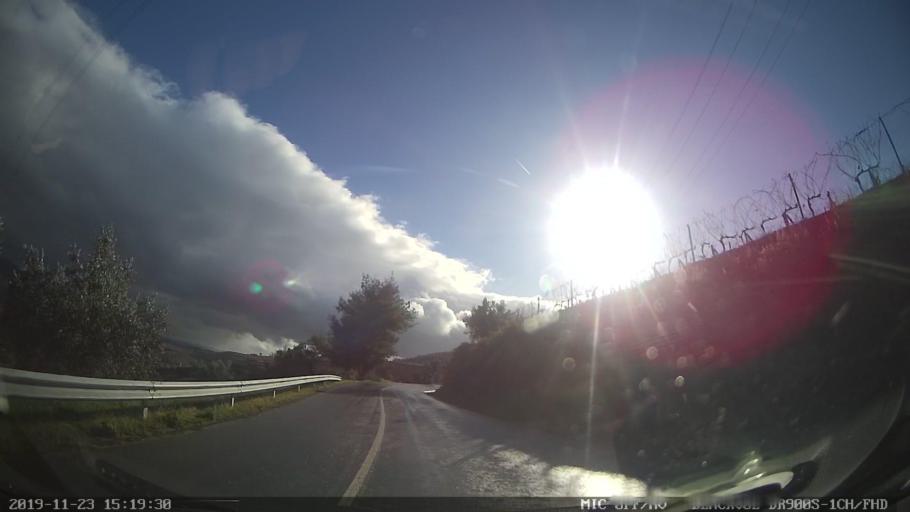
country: PT
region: Viseu
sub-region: Lamego
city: Lamego
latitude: 41.1170
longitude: -7.7898
